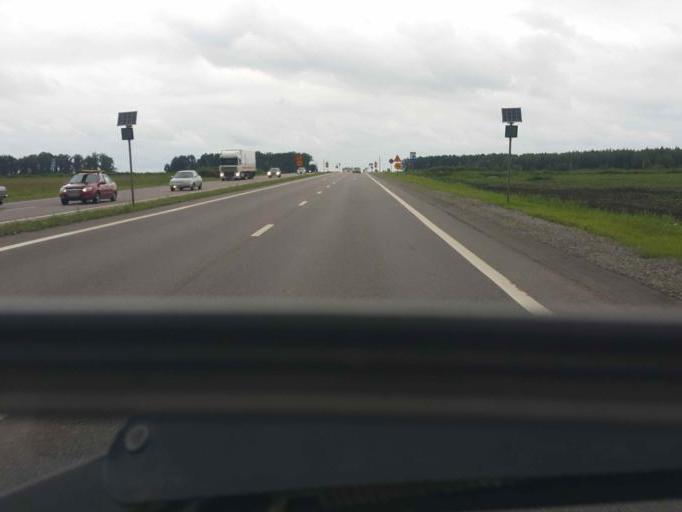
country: RU
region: Tambov
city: Zavoronezhskoye
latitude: 52.8892
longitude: 40.7042
